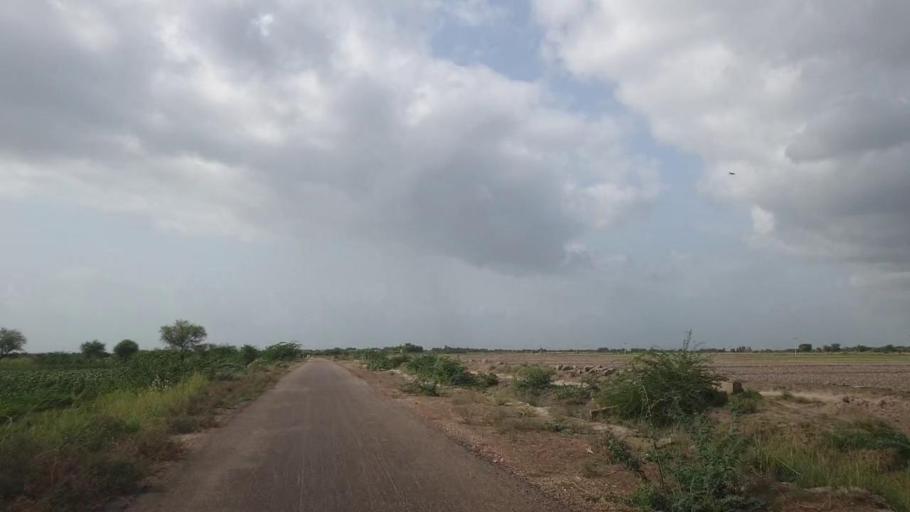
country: PK
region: Sindh
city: Kadhan
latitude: 24.5639
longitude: 69.0639
